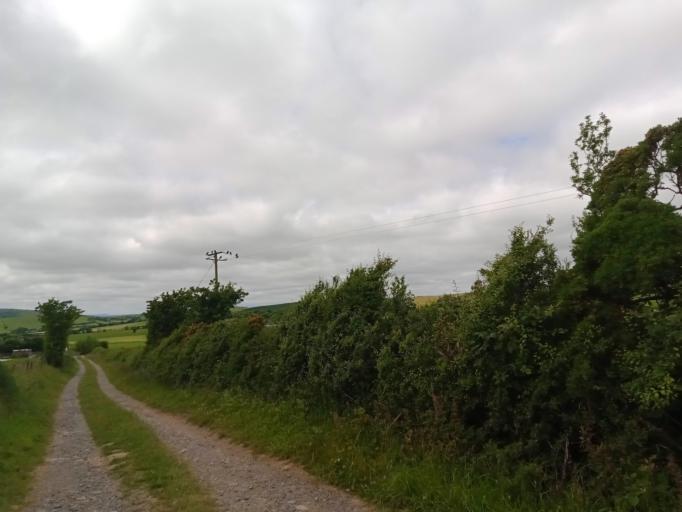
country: IE
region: Leinster
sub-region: Kilkenny
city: Ballyragget
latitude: 52.7943
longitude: -7.4583
